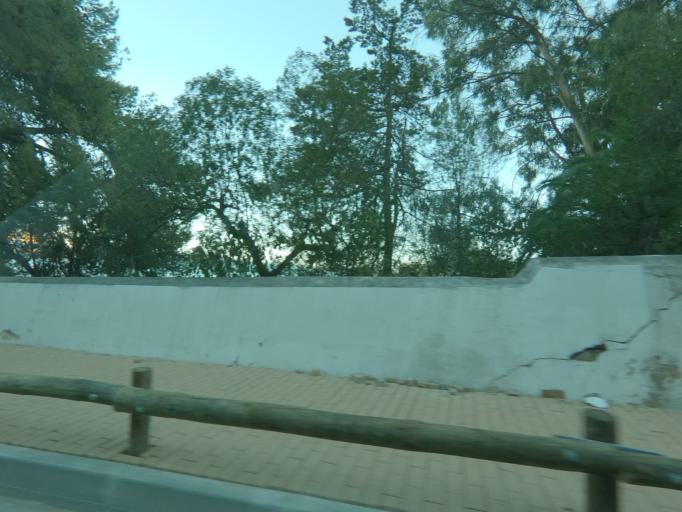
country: PT
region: Setubal
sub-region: Setubal
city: Setubal
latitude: 38.5160
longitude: -8.9086
